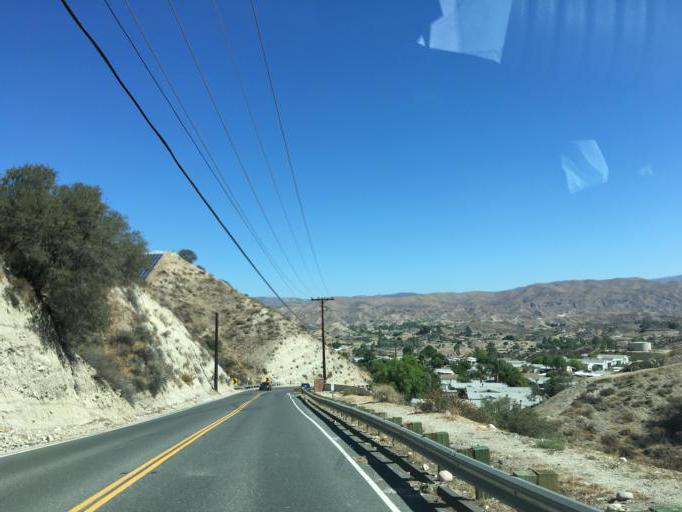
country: US
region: California
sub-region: Los Angeles County
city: Agua Dulce
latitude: 34.4449
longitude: -118.4205
